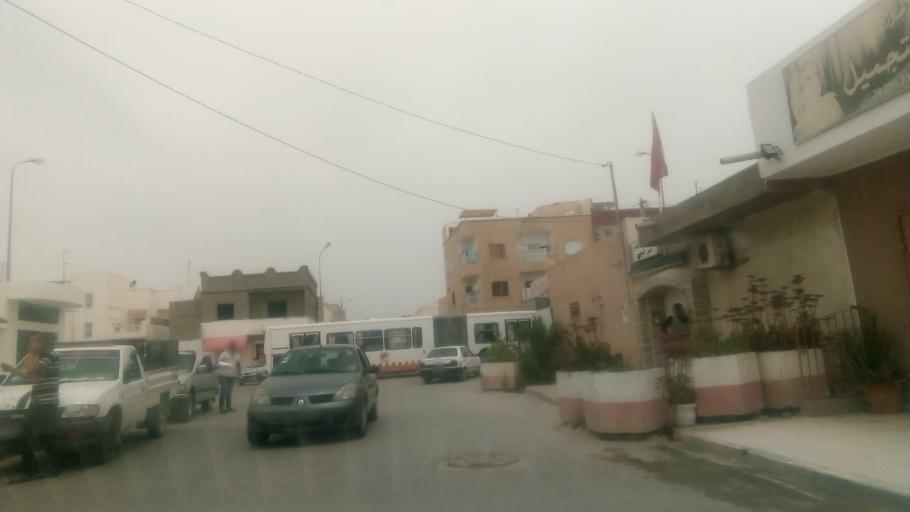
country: TN
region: Al Qayrawan
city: Kairouan
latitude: 35.6697
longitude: 10.0824
